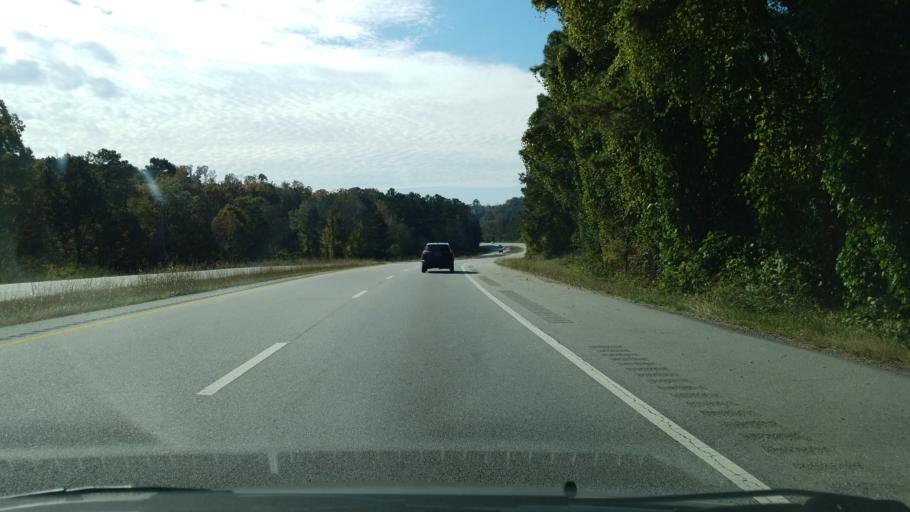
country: US
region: Tennessee
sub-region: Hamilton County
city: Harrison
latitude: 35.1322
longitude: -85.1225
